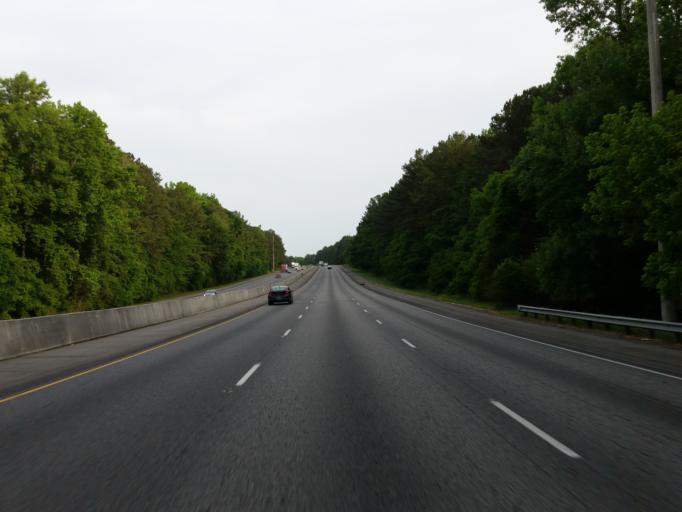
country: US
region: Georgia
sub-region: Bibb County
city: West Point
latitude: 32.9156
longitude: -83.7970
